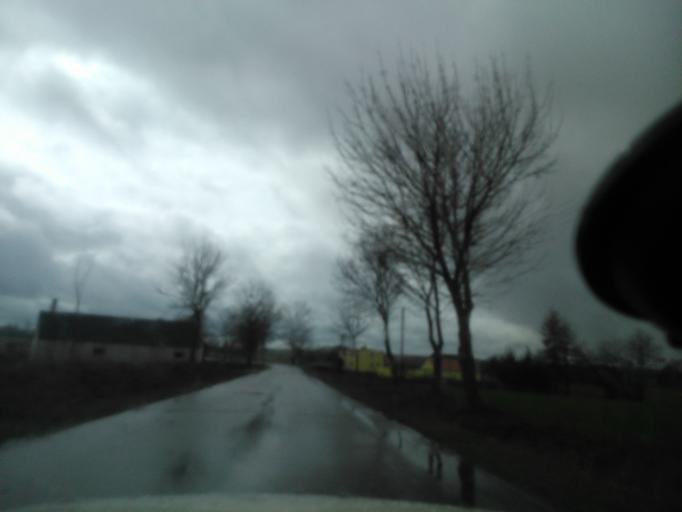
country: PL
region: Warmian-Masurian Voivodeship
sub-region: Powiat dzialdowski
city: Lidzbark
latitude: 53.3172
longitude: 19.8757
